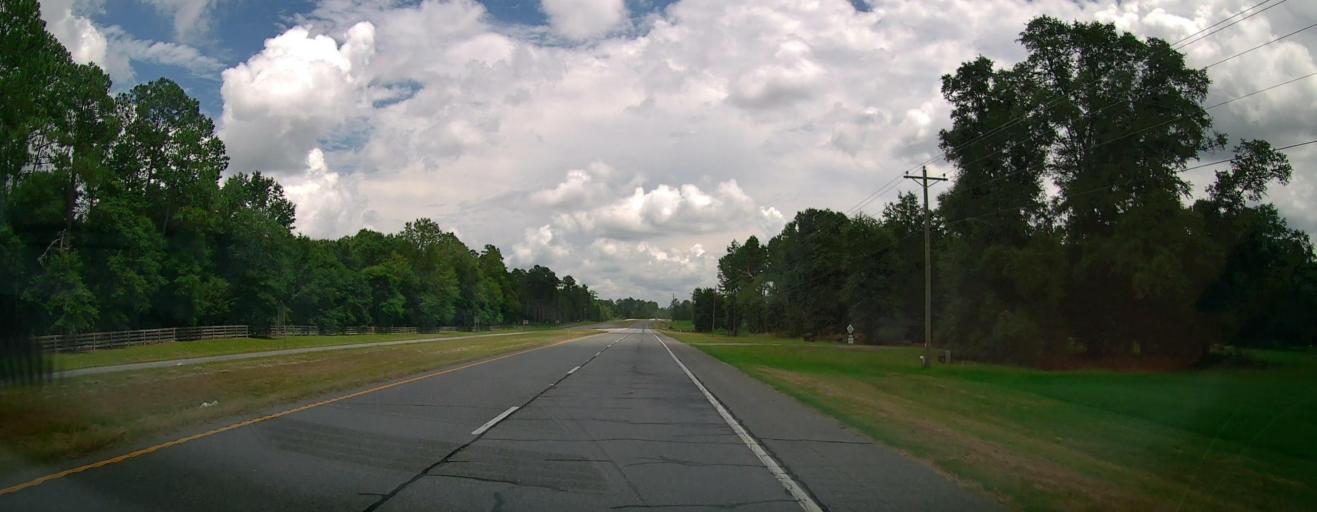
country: US
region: Georgia
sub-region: Pulaski County
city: Hawkinsville
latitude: 32.2730
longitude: -83.4202
